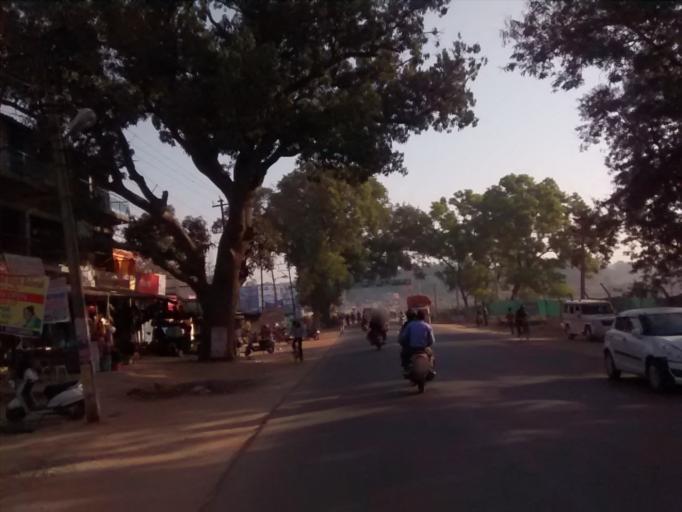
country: IN
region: Jharkhand
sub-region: Ranchi
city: Ranchi
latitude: 23.3866
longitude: 85.3726
